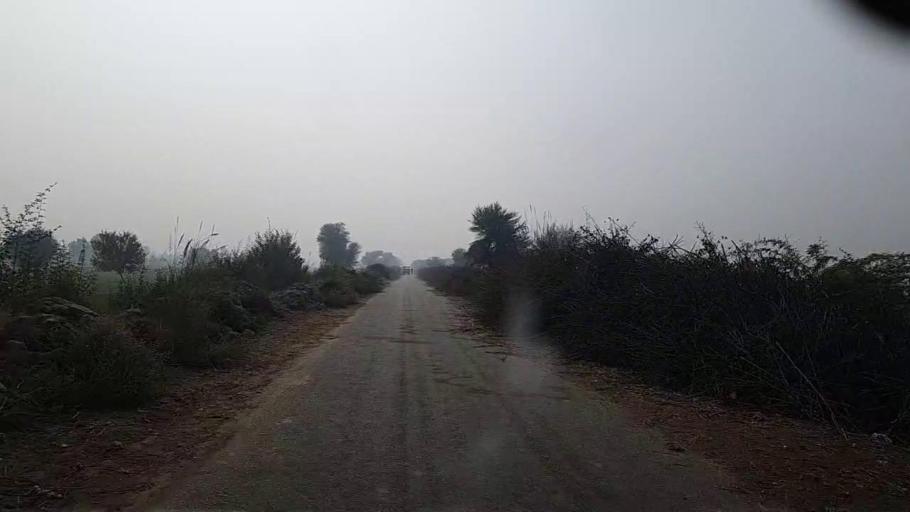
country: PK
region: Sindh
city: Kandiari
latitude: 26.9926
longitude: 68.6051
